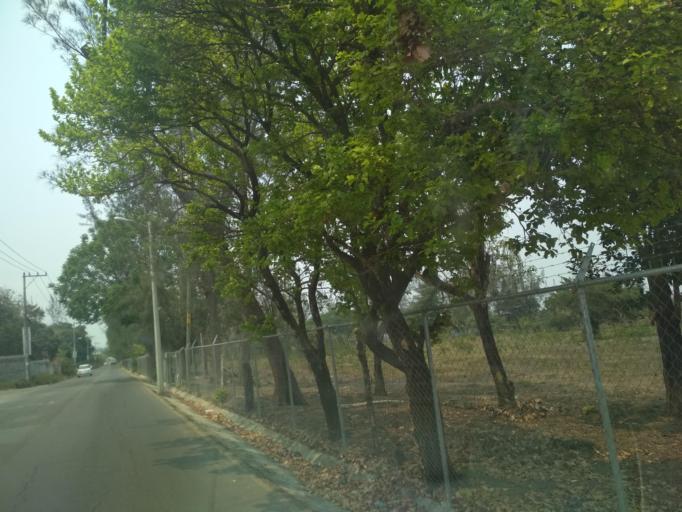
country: MX
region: Veracruz
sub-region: Veracruz
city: Las Amapolas
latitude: 19.1558
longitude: -96.2095
